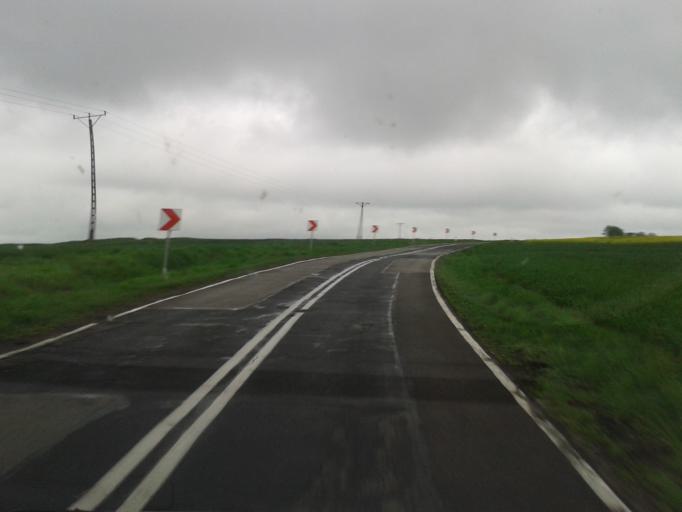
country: PL
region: Lublin Voivodeship
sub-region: Powiat hrubieszowski
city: Dolhobyczow
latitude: 50.5716
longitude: 23.9625
